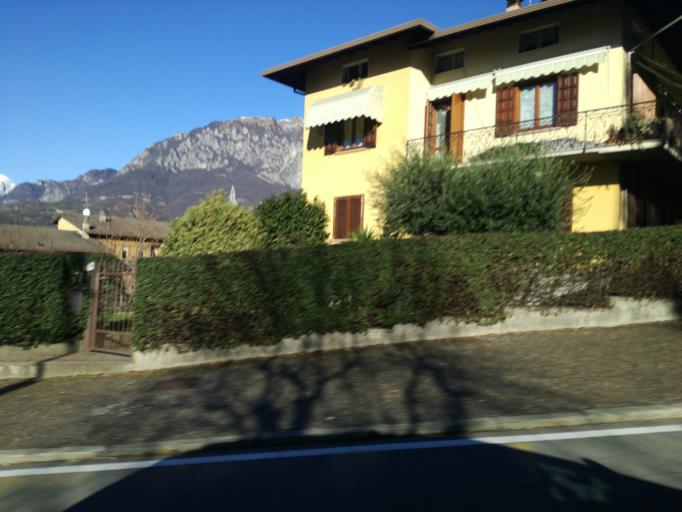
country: IT
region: Lombardy
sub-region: Provincia di Brescia
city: Gianico
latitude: 45.8650
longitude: 10.1775
